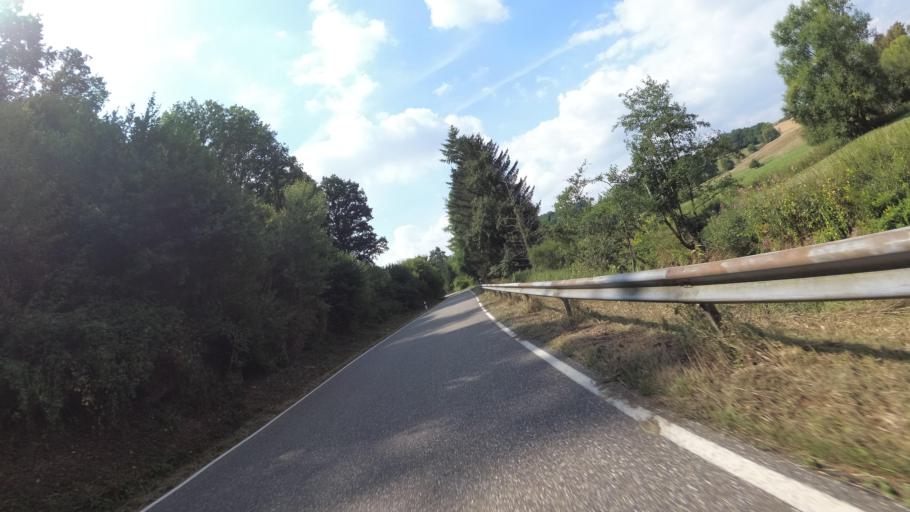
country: DE
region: Rheinland-Pfalz
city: Dietrichingen
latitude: 49.1943
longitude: 7.4161
